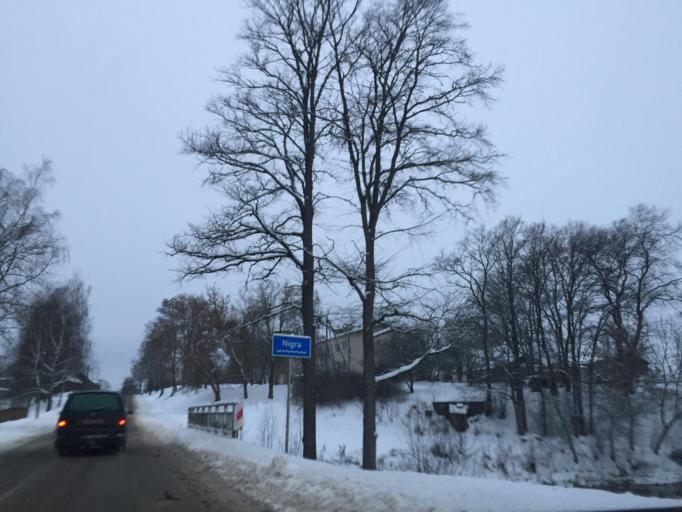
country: LV
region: Smiltene
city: Smiltene
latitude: 57.4371
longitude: 25.7855
